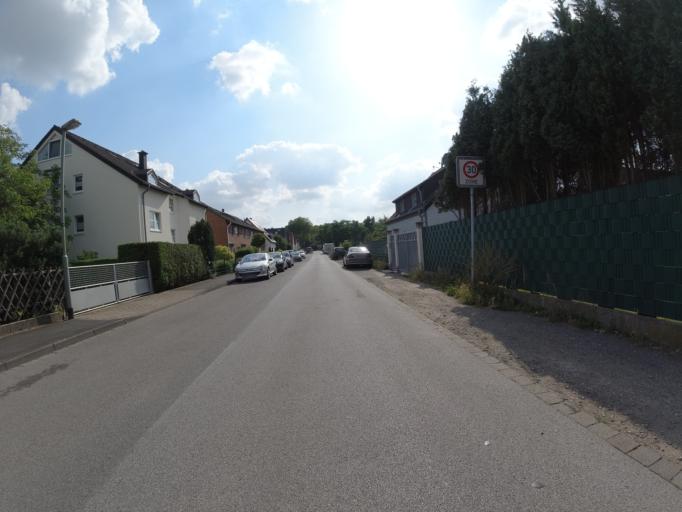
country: DE
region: North Rhine-Westphalia
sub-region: Regierungsbezirk Dusseldorf
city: Moers
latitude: 51.3963
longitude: 6.6695
